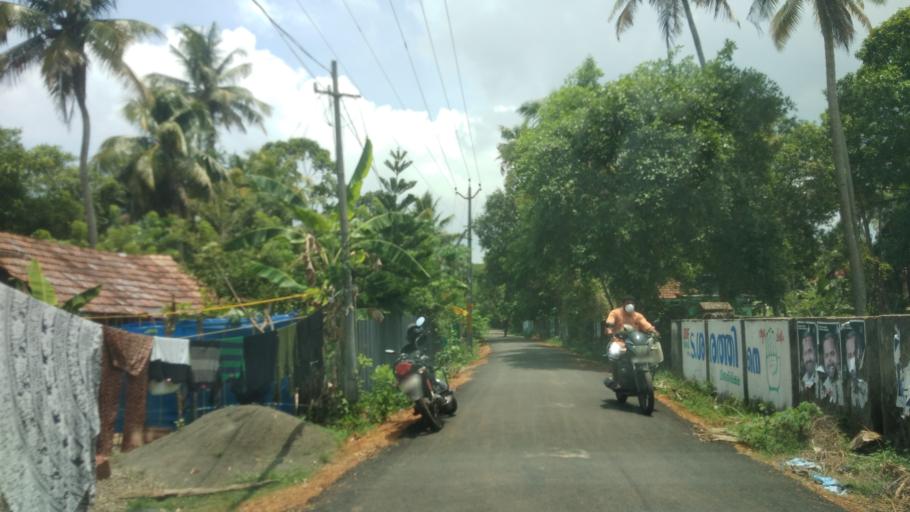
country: IN
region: Kerala
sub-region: Alappuzha
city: Shertallai
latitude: 9.6546
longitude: 76.3311
